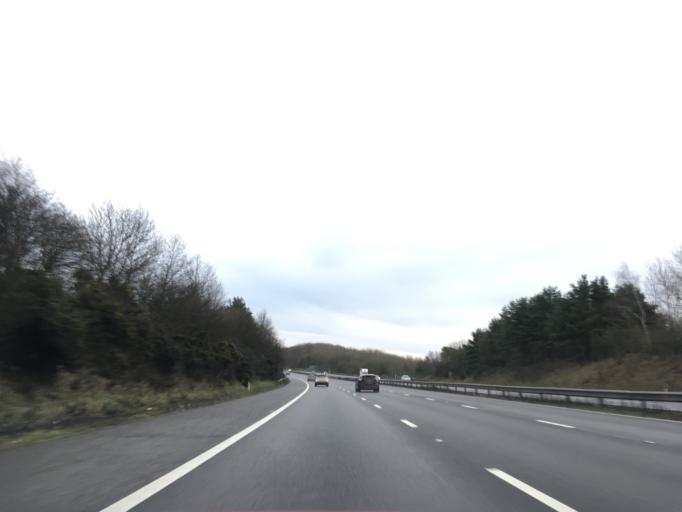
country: GB
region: England
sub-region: Worcestershire
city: Barnt Green
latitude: 52.3531
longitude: -2.0030
